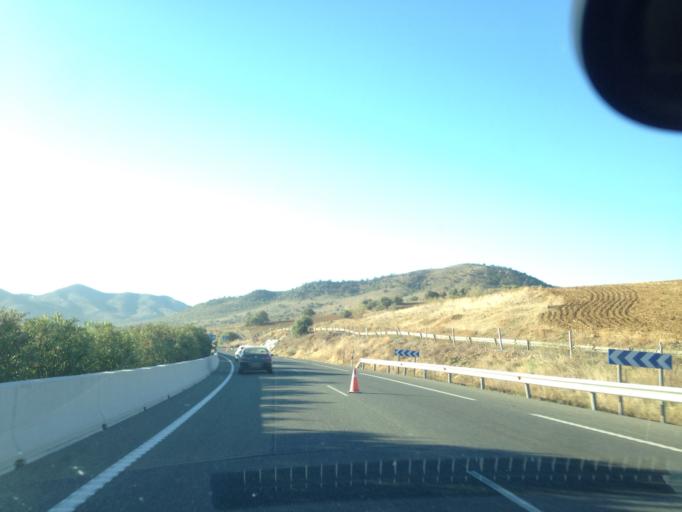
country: ES
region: Andalusia
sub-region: Provincia de Malaga
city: Casabermeja
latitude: 36.9324
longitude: -4.4457
